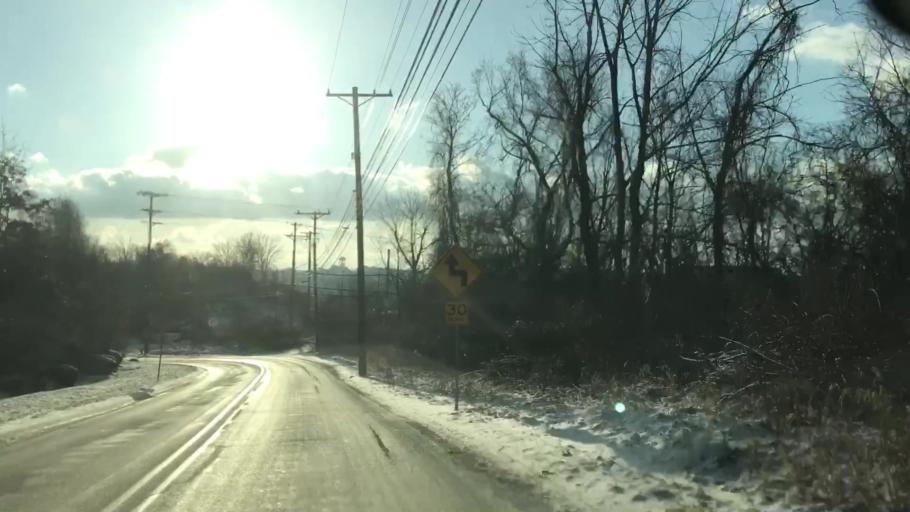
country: US
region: Pennsylvania
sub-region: Allegheny County
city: Coraopolis
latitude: 40.4670
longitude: -80.1794
